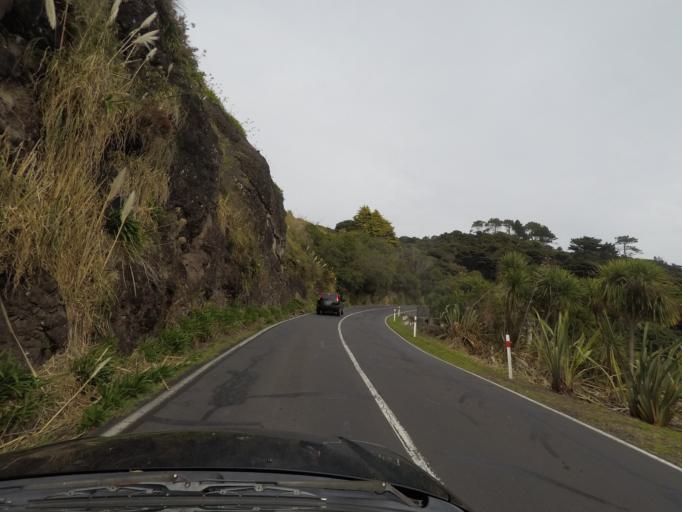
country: NZ
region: Auckland
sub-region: Auckland
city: Muriwai Beach
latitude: -36.9604
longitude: 174.4773
